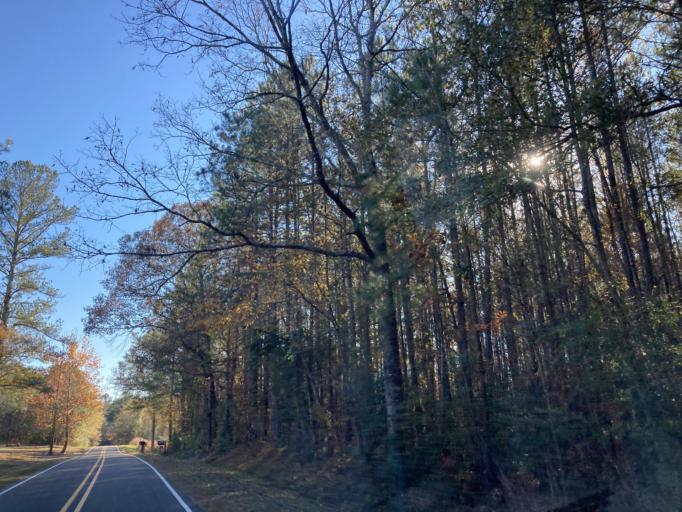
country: US
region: Mississippi
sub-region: Lamar County
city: Sumrall
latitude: 31.3572
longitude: -89.5693
